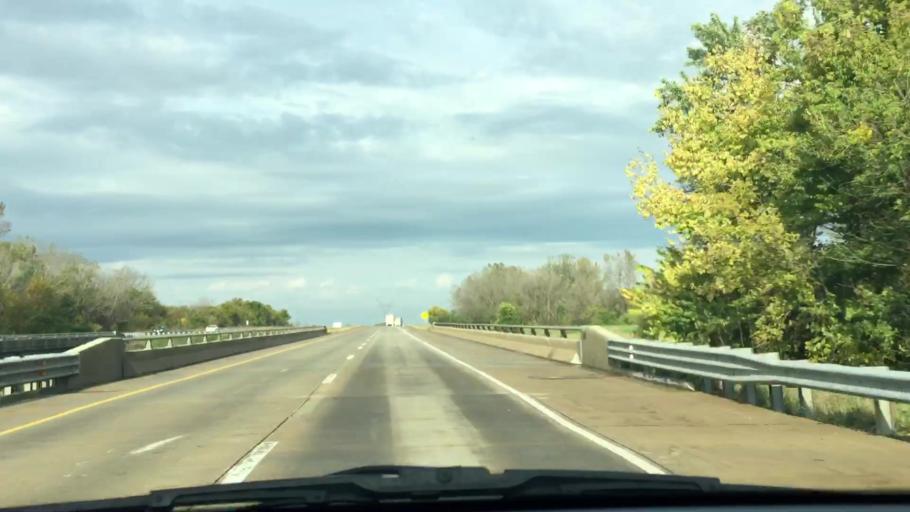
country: US
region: Illinois
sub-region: Whiteside County
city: Sterling
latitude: 41.7600
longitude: -89.7841
